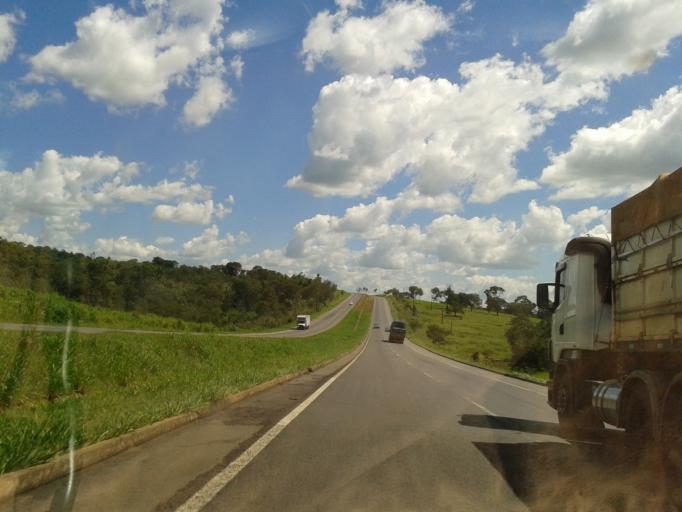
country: BR
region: Goias
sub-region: Piracanjuba
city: Piracanjuba
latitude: -17.3547
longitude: -49.2482
